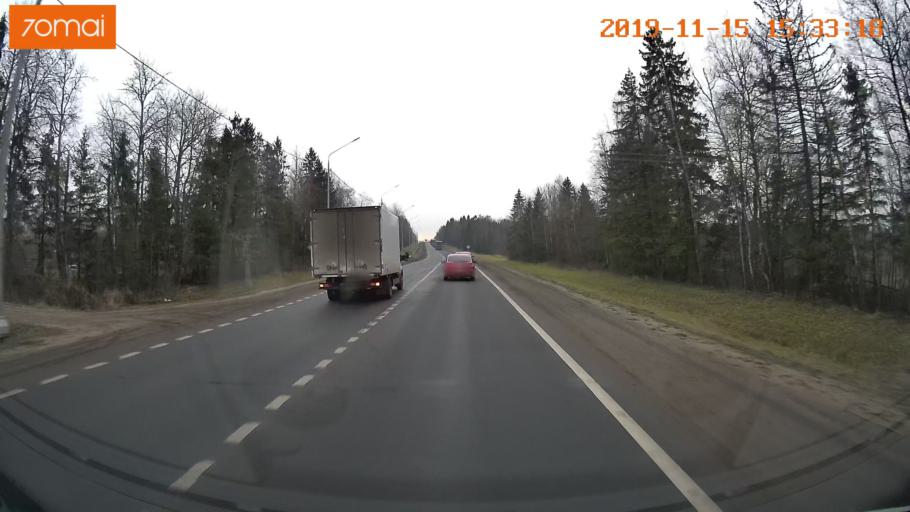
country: RU
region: Jaroslavl
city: Danilov
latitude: 58.0819
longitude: 40.0933
